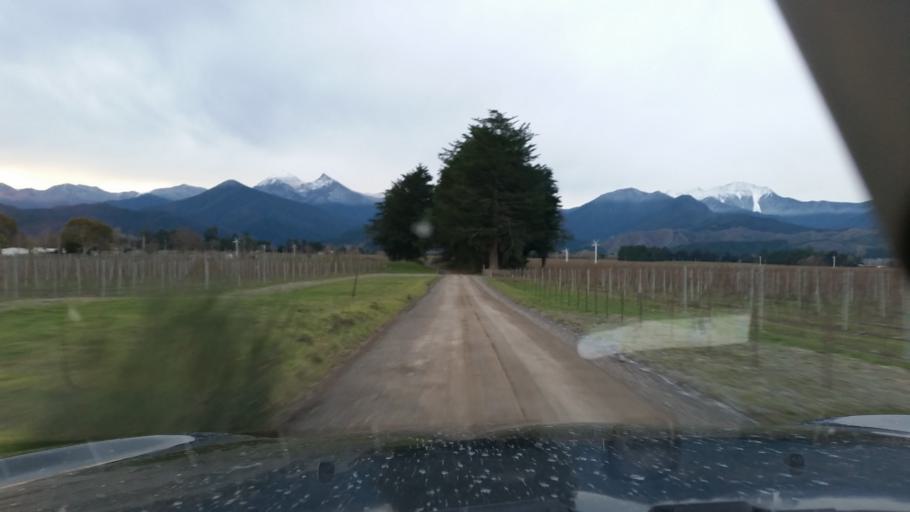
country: NZ
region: Nelson
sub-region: Nelson City
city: Nelson
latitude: -41.5840
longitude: 173.5103
